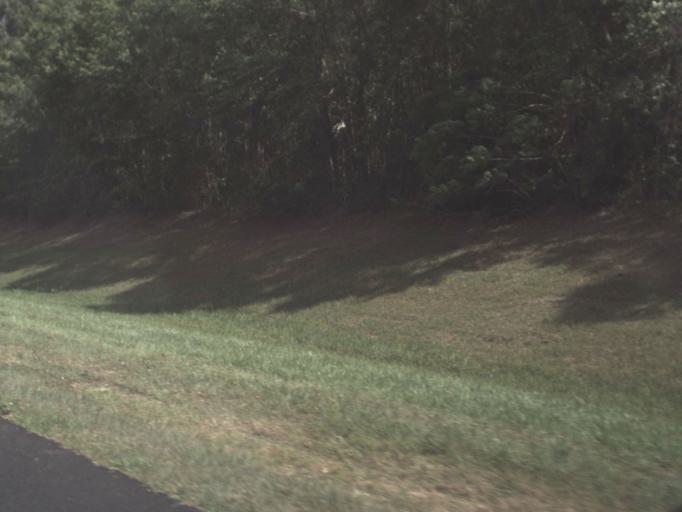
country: US
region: Florida
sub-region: Levy County
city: Williston
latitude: 29.2590
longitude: -82.3177
